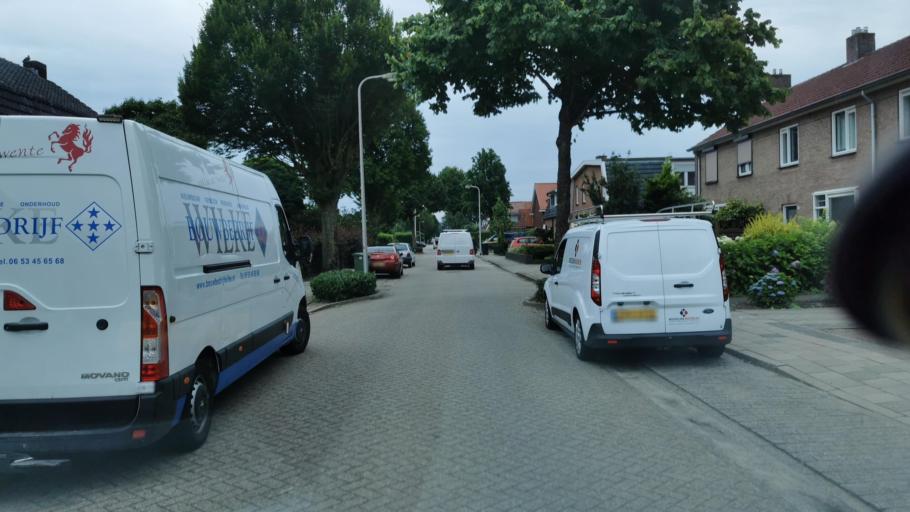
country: DE
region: North Rhine-Westphalia
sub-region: Regierungsbezirk Munster
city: Gronau
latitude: 52.2381
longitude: 7.0376
